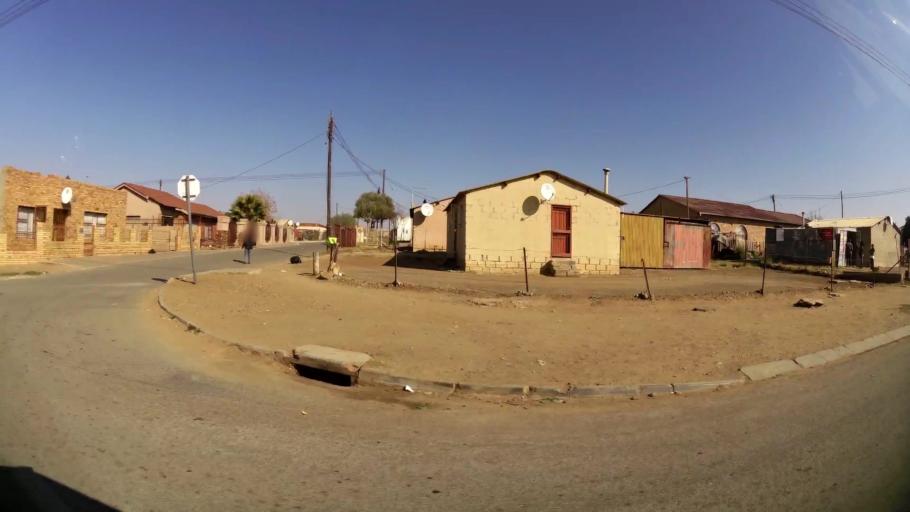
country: ZA
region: Orange Free State
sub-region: Mangaung Metropolitan Municipality
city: Bloemfontein
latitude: -29.1795
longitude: 26.2426
